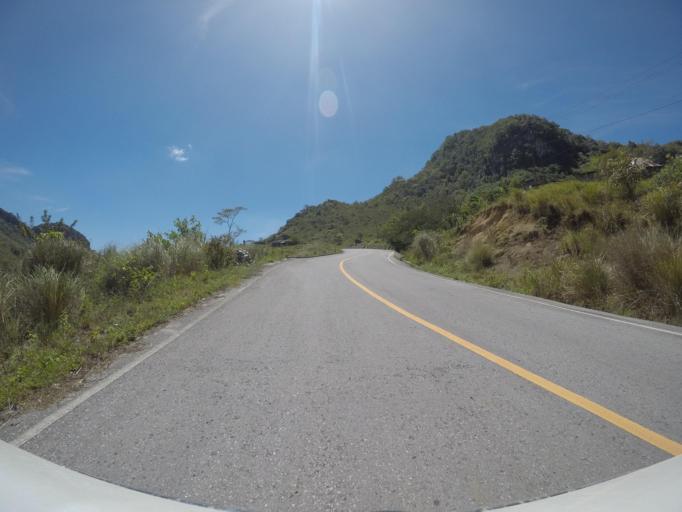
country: TL
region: Manatuto
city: Manatuto
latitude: -8.7636
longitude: 125.9681
